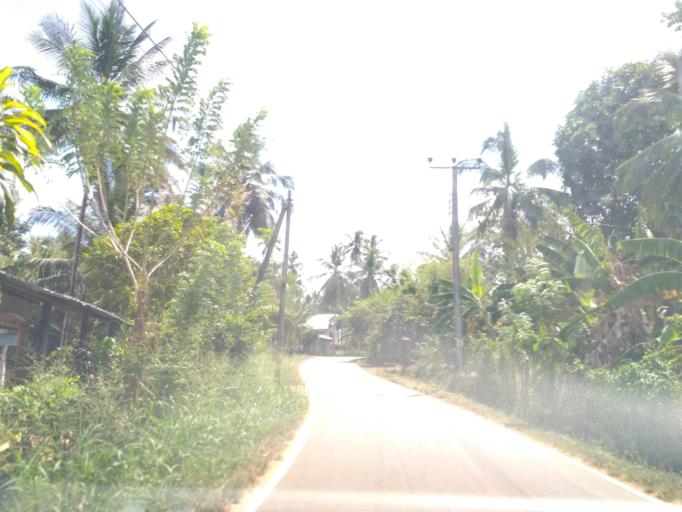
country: LK
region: North Western
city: Kuliyapitiya
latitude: 7.3313
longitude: 80.0632
